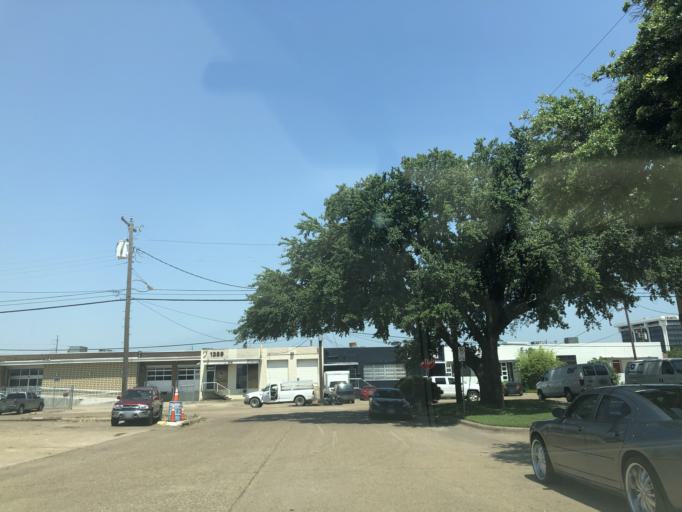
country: US
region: Texas
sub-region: Dallas County
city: Dallas
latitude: 32.8016
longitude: -96.8380
